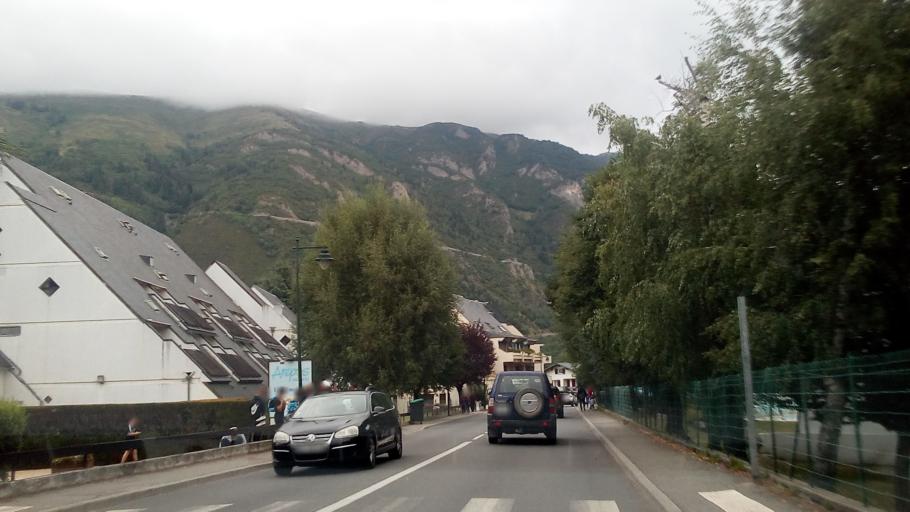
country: FR
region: Midi-Pyrenees
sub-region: Departement des Hautes-Pyrenees
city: Saint-Lary-Soulan
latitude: 42.8201
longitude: 0.3227
